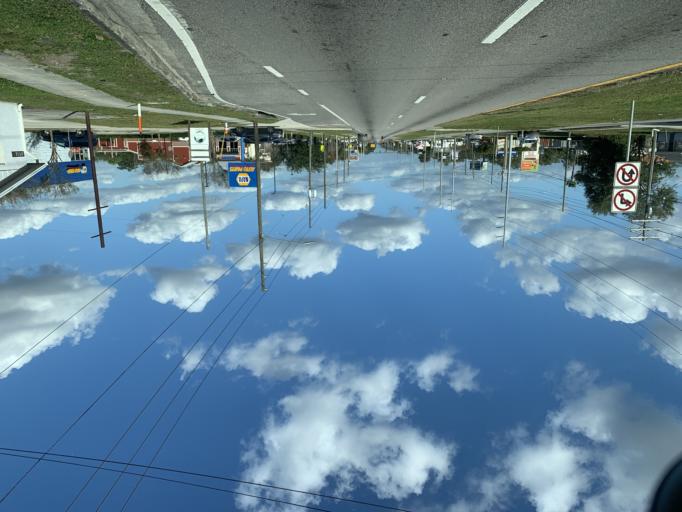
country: US
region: Florida
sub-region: Orange County
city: Lockhart
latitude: 28.6160
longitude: -81.4148
